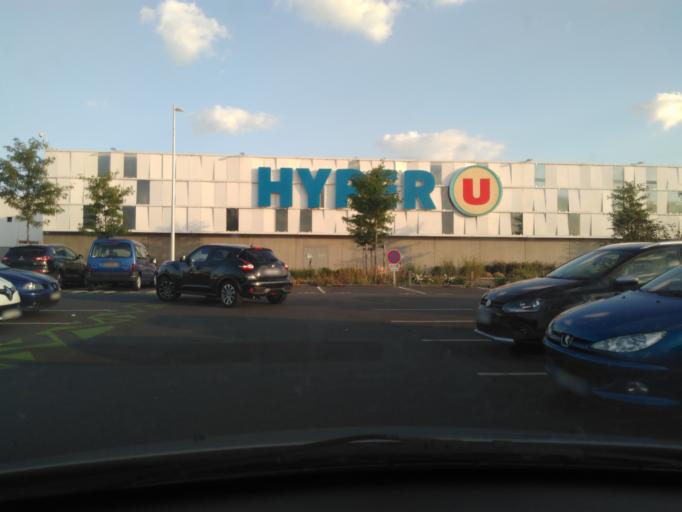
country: FR
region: Poitou-Charentes
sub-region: Departement de la Charente-Maritime
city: Puilboreau
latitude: 46.1740
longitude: -1.1171
